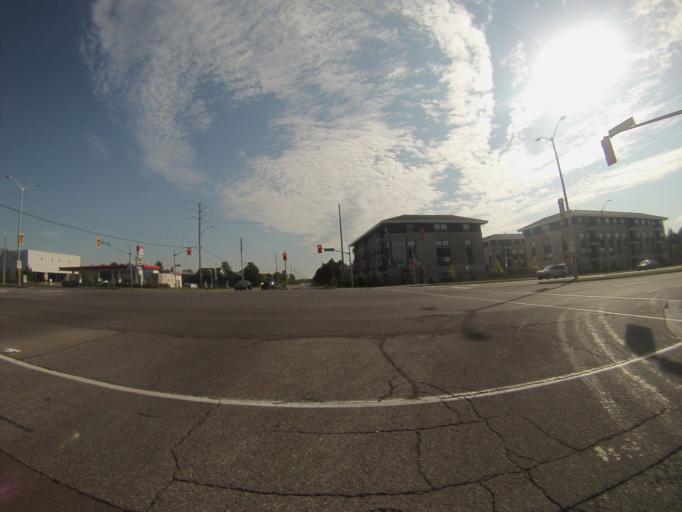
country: CA
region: Ontario
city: Ottawa
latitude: 45.3732
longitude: -75.6246
